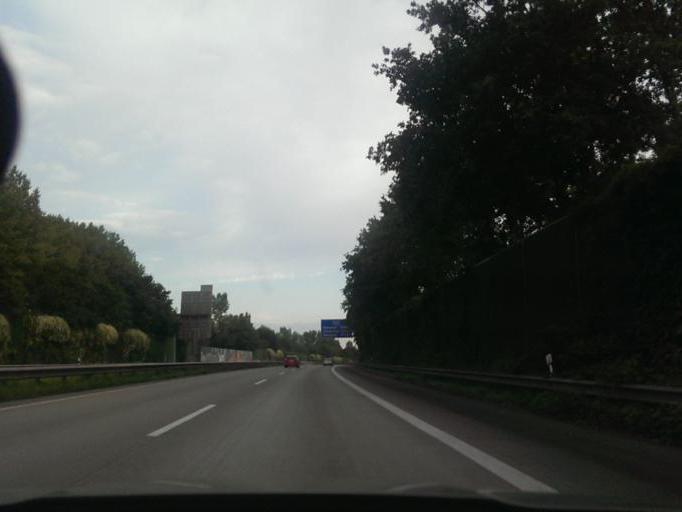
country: DE
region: Lower Saxony
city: Lilienthal
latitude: 53.1041
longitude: 8.8800
